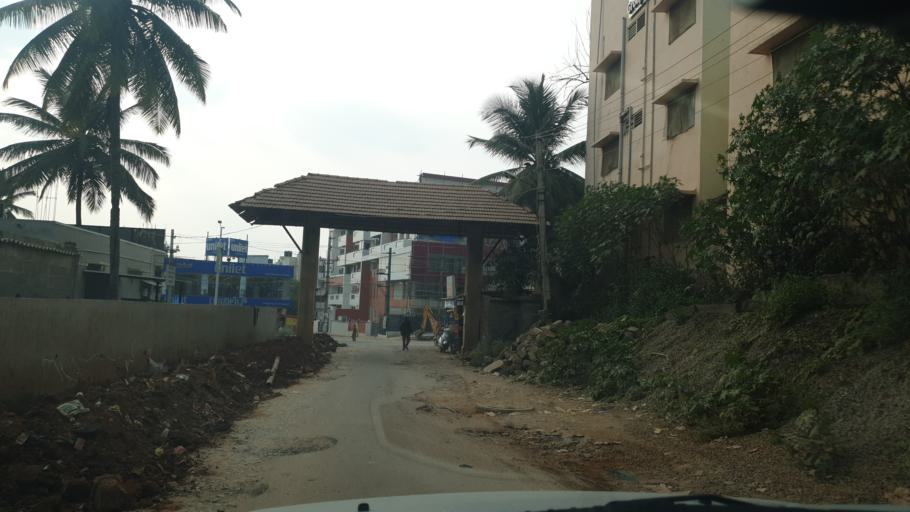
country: IN
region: Karnataka
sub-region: Bangalore Urban
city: Yelahanka
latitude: 13.0582
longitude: 77.6492
